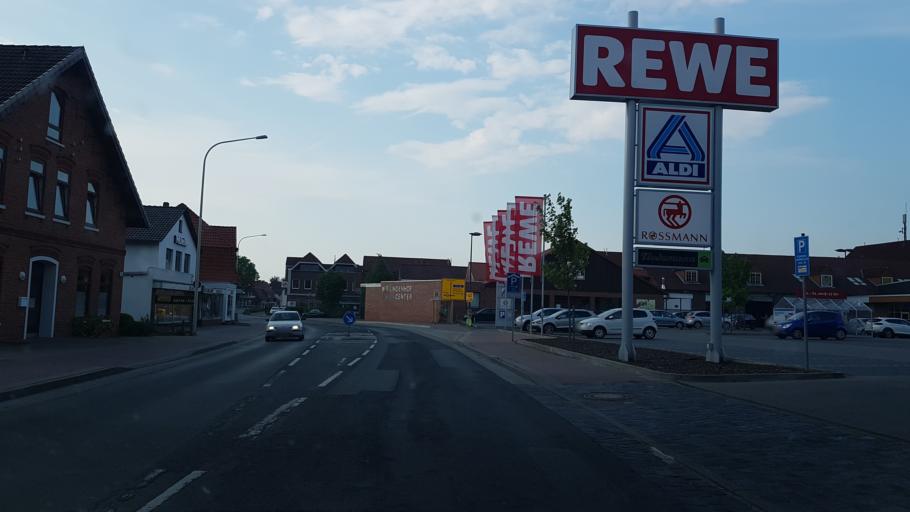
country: DE
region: Lower Saxony
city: Langen
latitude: 53.6062
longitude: 8.5949
